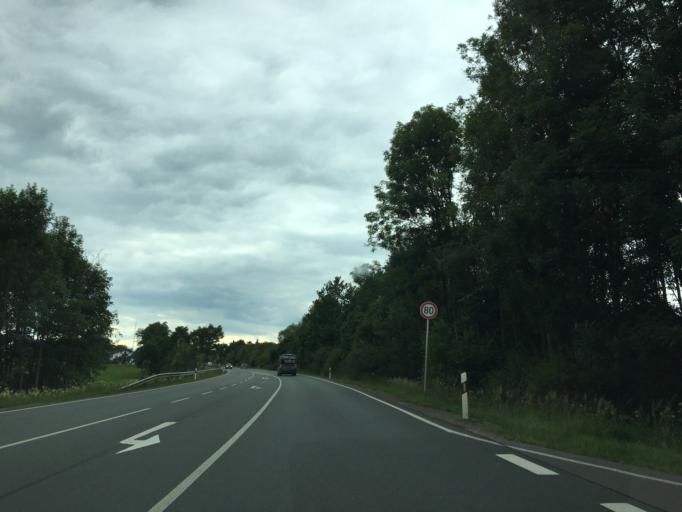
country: DE
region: Bavaria
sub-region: Upper Bavaria
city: Miesbach
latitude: 47.7838
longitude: 11.8163
